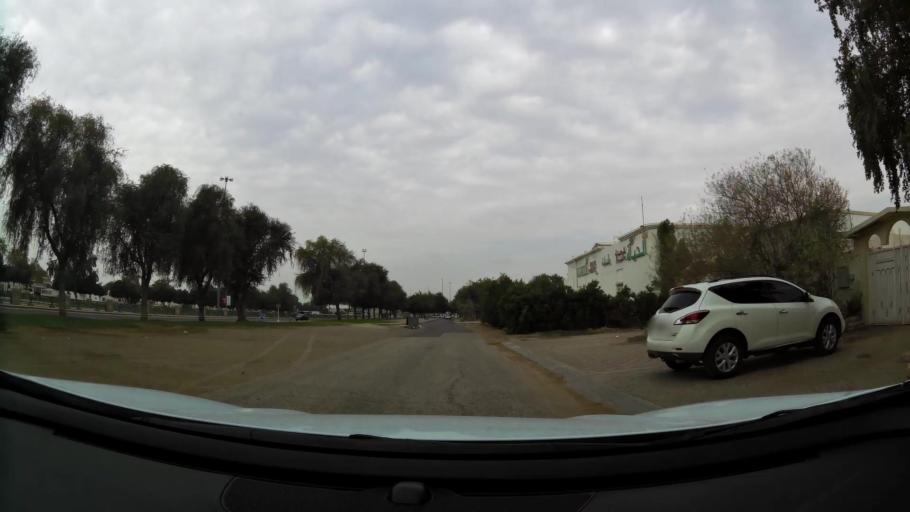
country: AE
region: Abu Dhabi
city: Al Ain
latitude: 24.2250
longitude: 55.7406
